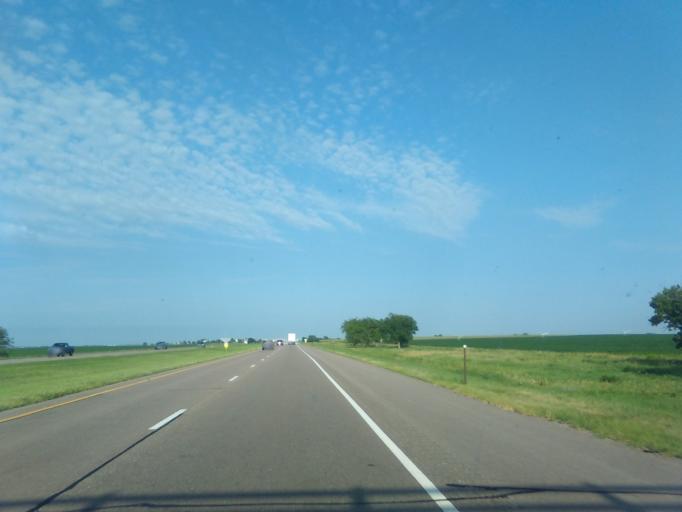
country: US
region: Nebraska
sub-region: York County
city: York
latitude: 40.8213
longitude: -97.7113
